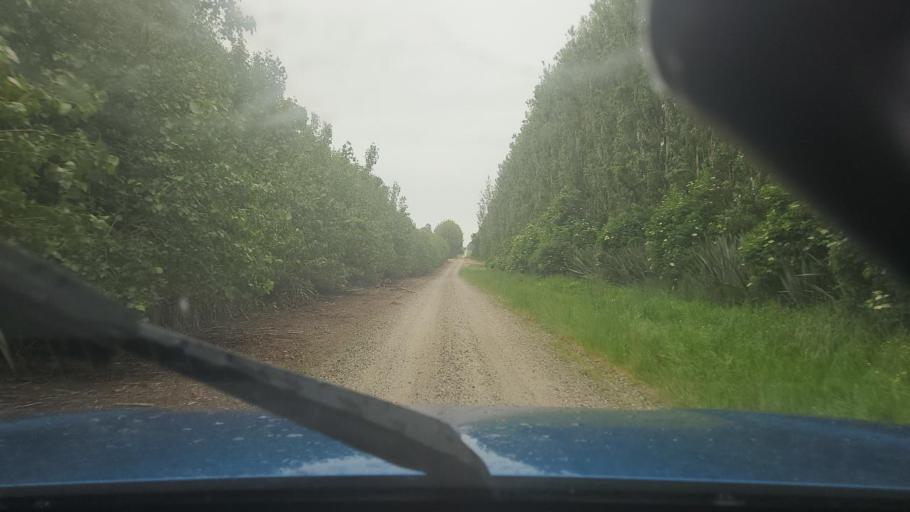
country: NZ
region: Southland
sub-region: Invercargill City
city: Invercargill
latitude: -46.3707
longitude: 168.5895
